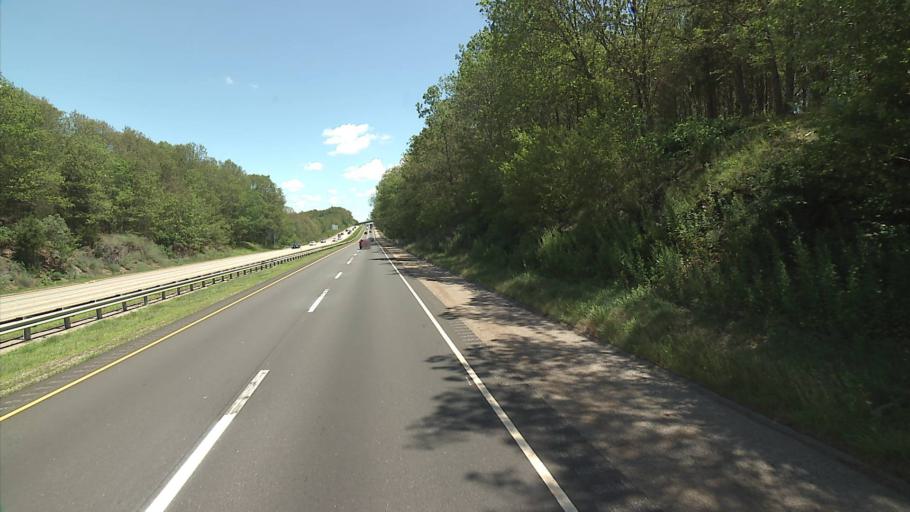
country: US
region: Connecticut
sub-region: New London County
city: Jewett City
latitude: 41.5976
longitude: -71.9635
